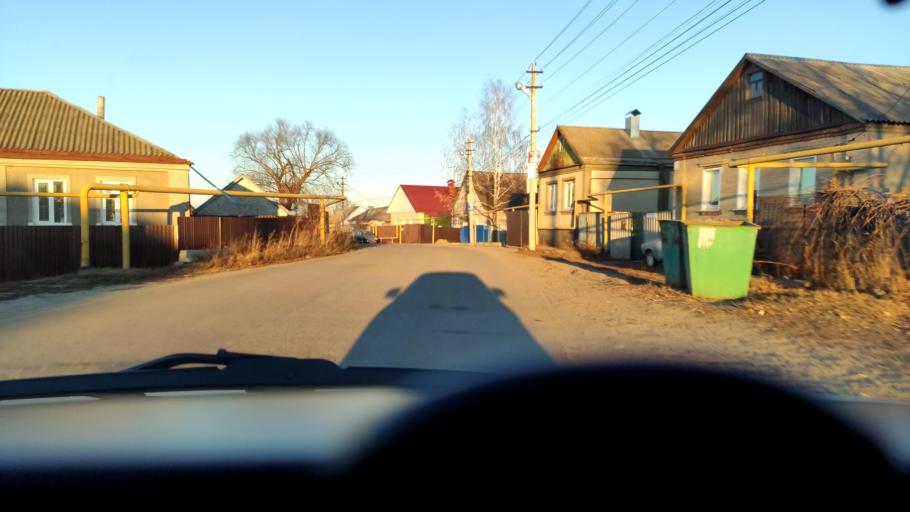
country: RU
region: Voronezj
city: Podgornoye
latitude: 51.7409
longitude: 39.1466
